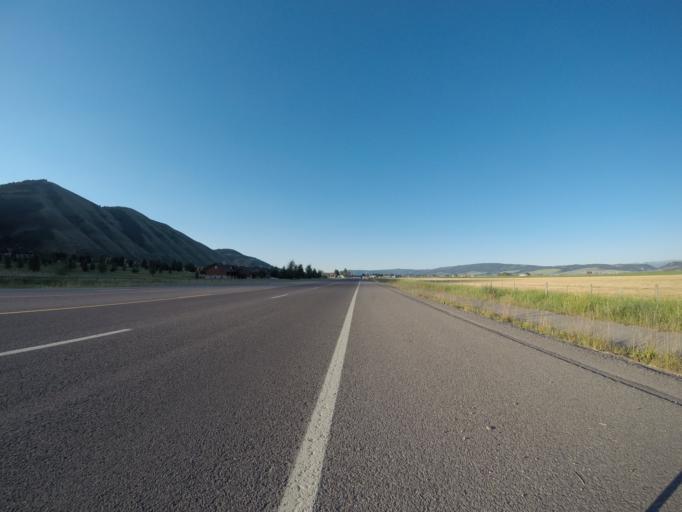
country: US
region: Wyoming
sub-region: Lincoln County
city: Afton
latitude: 42.7054
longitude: -110.9335
